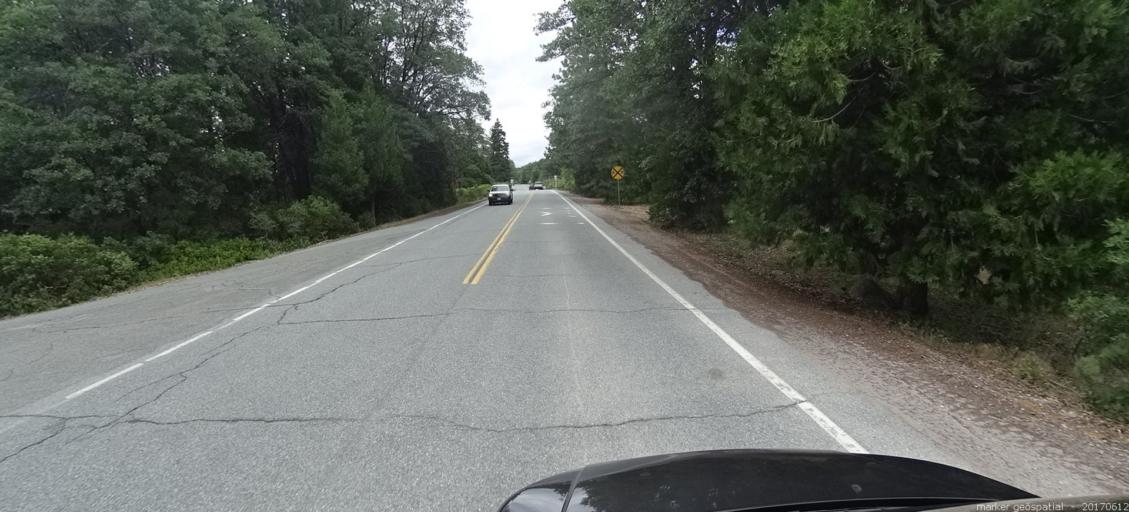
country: US
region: California
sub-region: Siskiyou County
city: Mount Shasta
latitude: 41.3245
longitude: -122.3062
